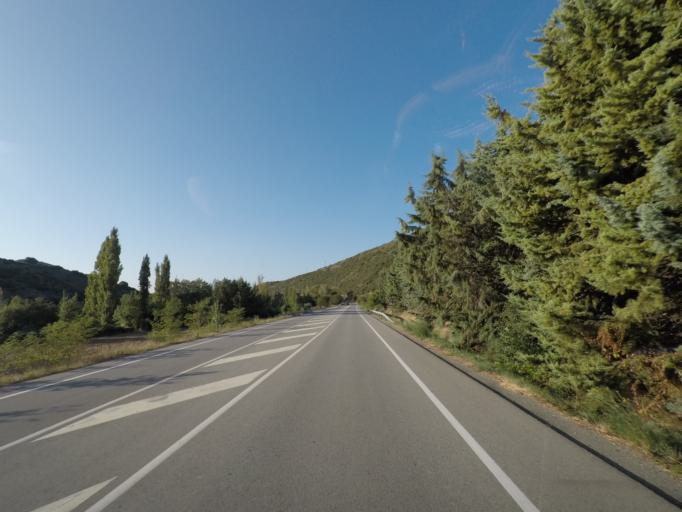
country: ES
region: Navarre
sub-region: Provincia de Navarra
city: Liedena
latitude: 42.6094
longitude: -1.2779
